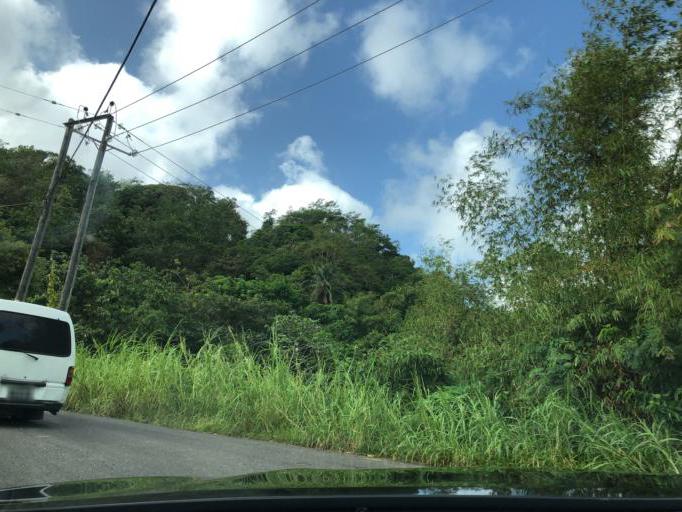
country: LC
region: Castries Quarter
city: Bisee
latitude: 13.9909
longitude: -60.9598
